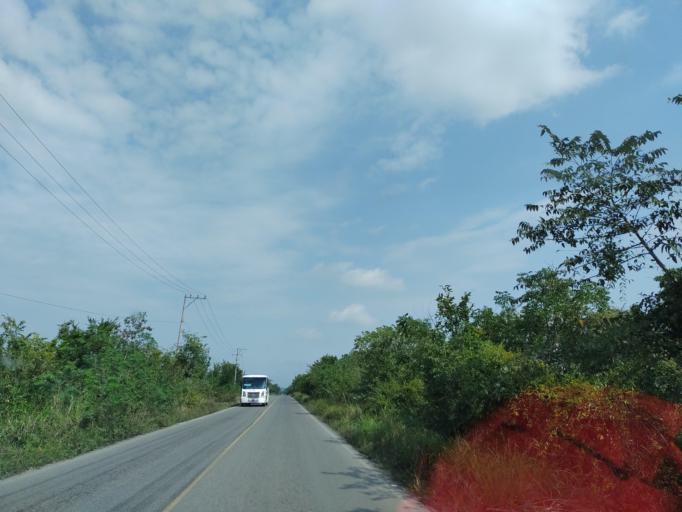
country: MX
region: Puebla
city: Espinal
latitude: 20.2794
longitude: -97.3308
